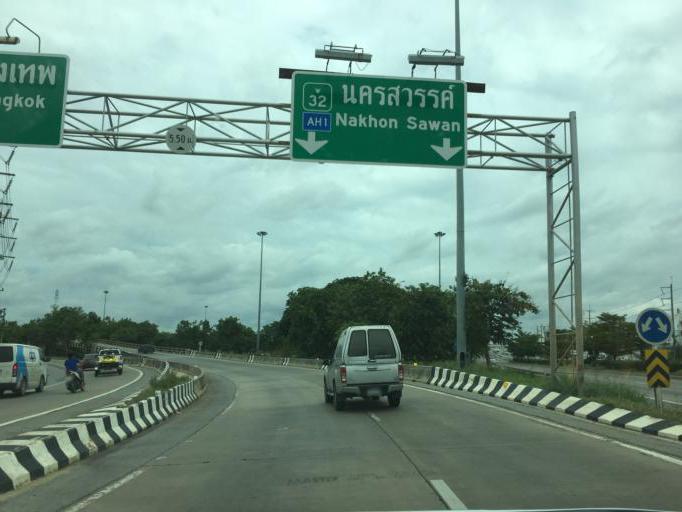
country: TH
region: Phra Nakhon Si Ayutthaya
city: Phra Nakhon Si Ayutthaya
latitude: 14.3362
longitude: 100.6172
